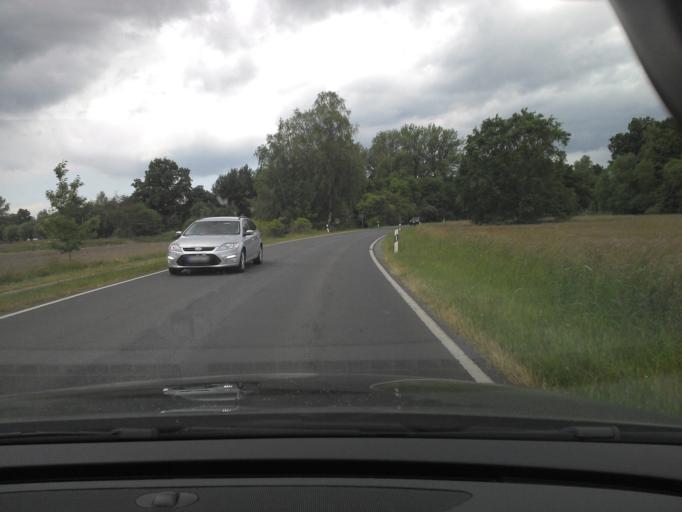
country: DE
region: Brandenburg
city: Burg
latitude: 51.8495
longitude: 14.1523
